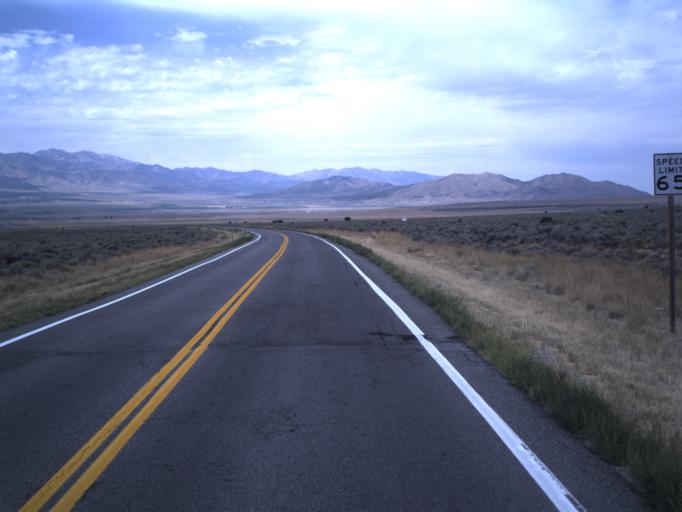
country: US
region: Utah
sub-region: Tooele County
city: Tooele
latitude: 40.3553
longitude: -112.3150
